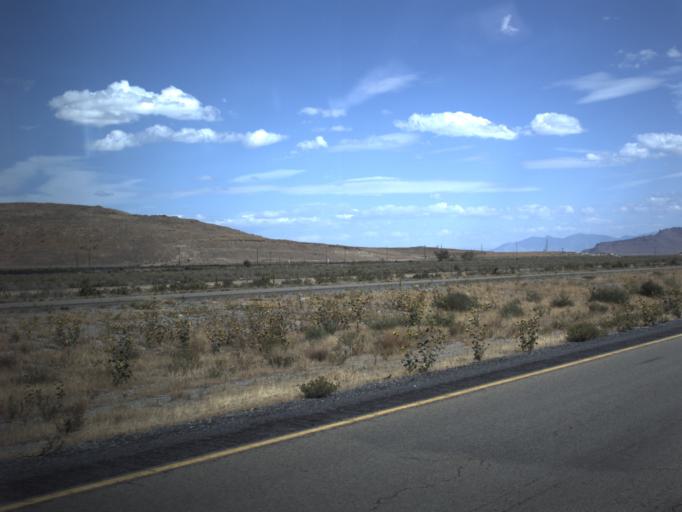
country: US
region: Utah
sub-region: Tooele County
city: Grantsville
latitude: 40.7691
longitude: -112.7933
